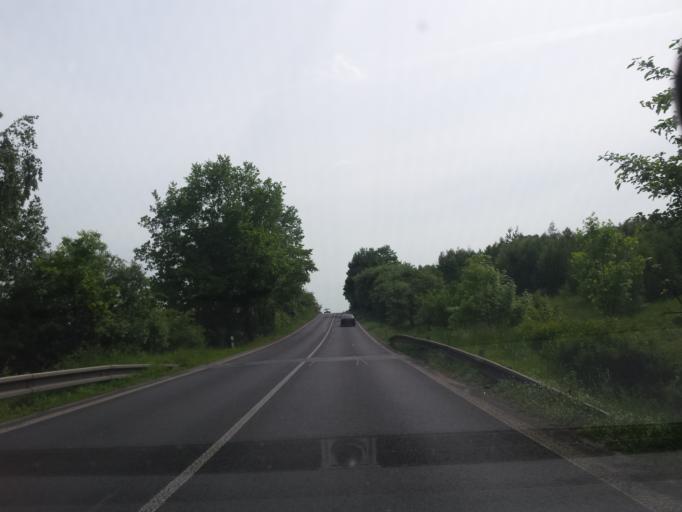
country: CZ
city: Novy Bor
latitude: 50.7390
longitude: 14.5511
